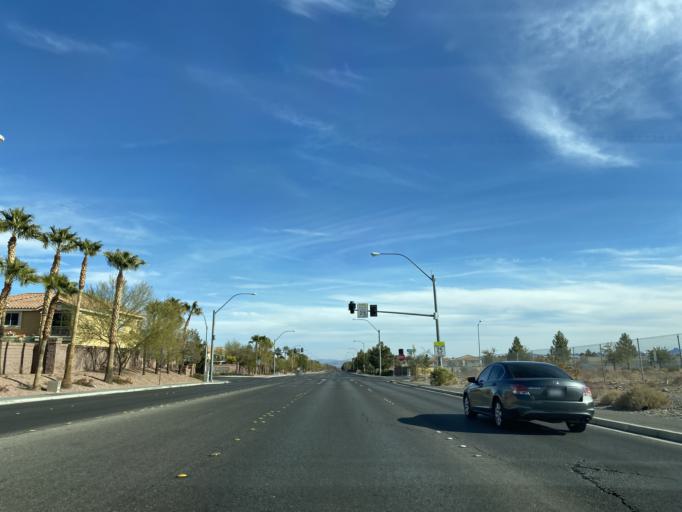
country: US
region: Nevada
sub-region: Clark County
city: Enterprise
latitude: 36.0488
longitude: -115.2352
